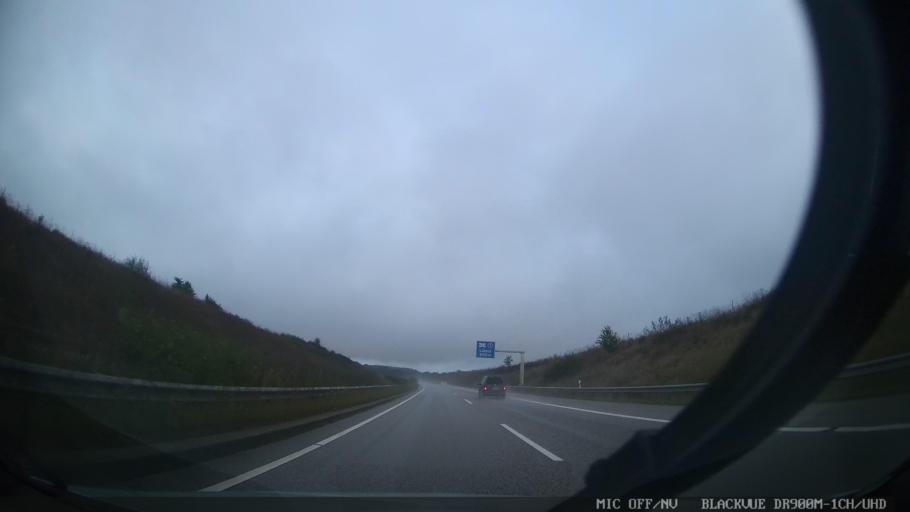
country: DE
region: Schleswig-Holstein
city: Badendorf
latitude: 53.8684
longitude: 10.5609
